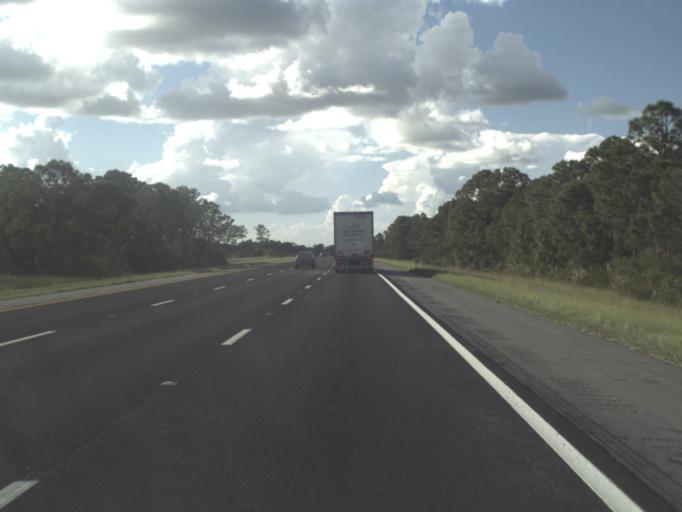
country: US
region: Florida
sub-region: Lee County
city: Suncoast Estates
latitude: 26.7990
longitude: -81.9139
